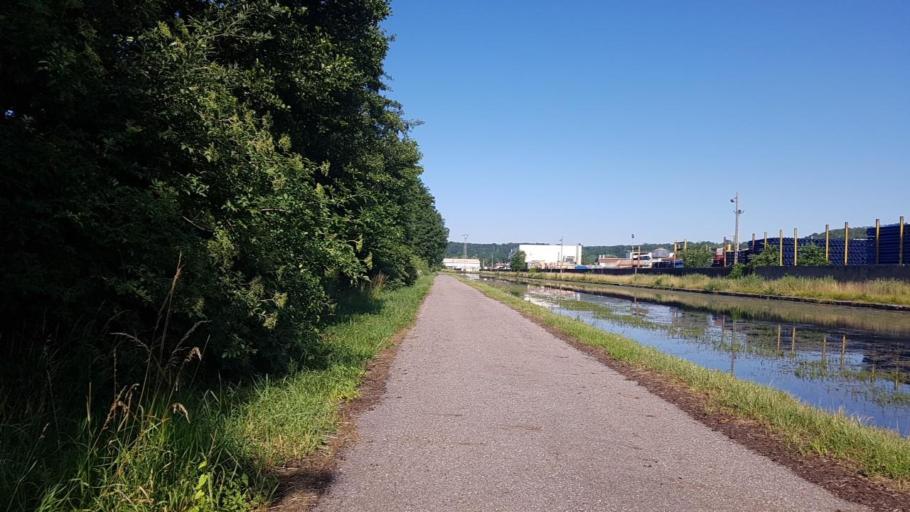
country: FR
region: Lorraine
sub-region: Departement de Meurthe-et-Moselle
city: Foug
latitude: 48.6757
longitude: 5.8064
